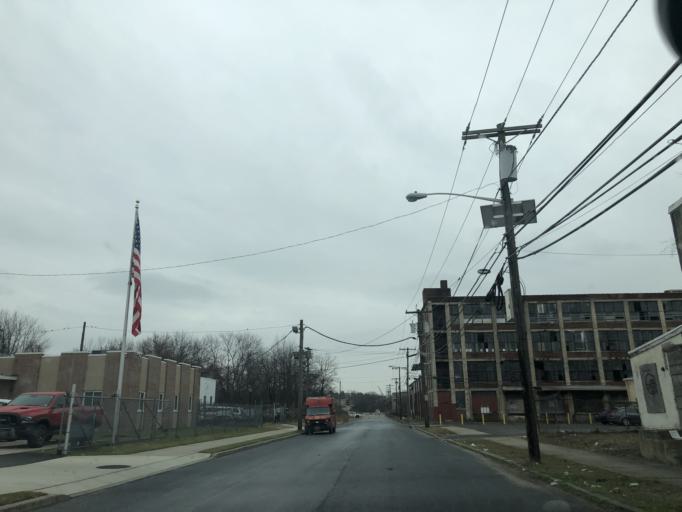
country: US
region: New Jersey
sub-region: Camden County
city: Camden
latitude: 39.9439
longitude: -75.1000
